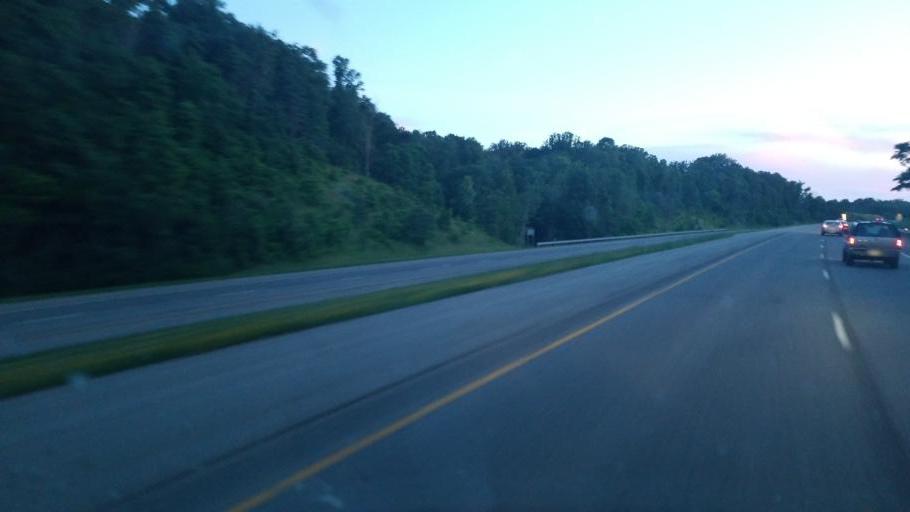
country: US
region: Ohio
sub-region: Summit County
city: Peninsula
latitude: 41.2576
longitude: -81.5649
